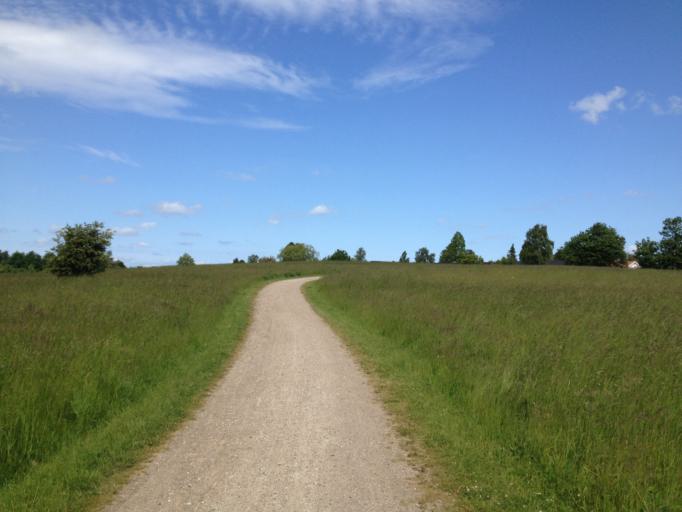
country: DK
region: Capital Region
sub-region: Fredensborg Kommune
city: Niva
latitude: 55.9302
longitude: 12.4908
